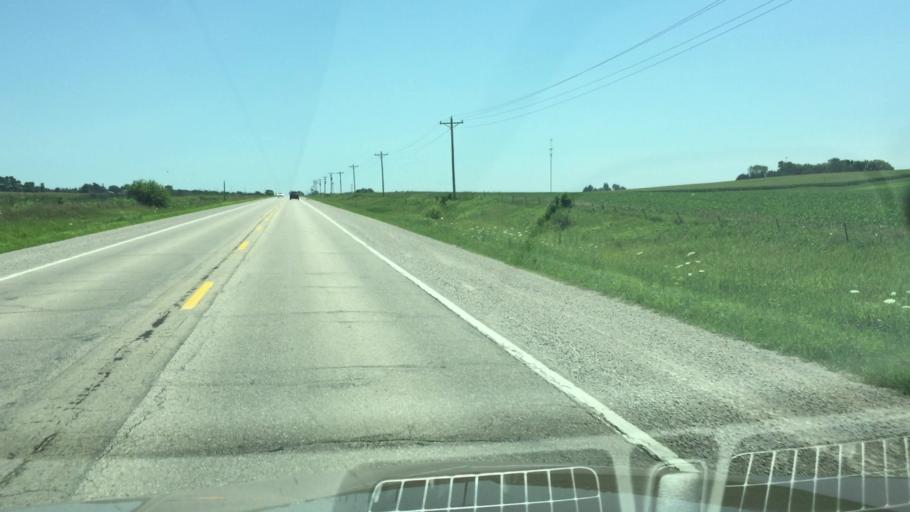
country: US
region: Iowa
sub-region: Cedar County
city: Mechanicsville
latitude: 41.9105
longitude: -91.2867
